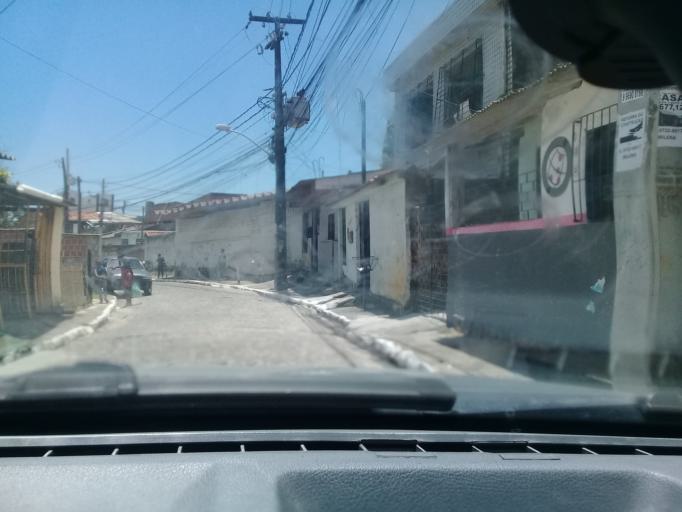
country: BR
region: Pernambuco
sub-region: Jaboatao Dos Guararapes
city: Jaboatao dos Guararapes
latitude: -8.1271
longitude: -34.9530
